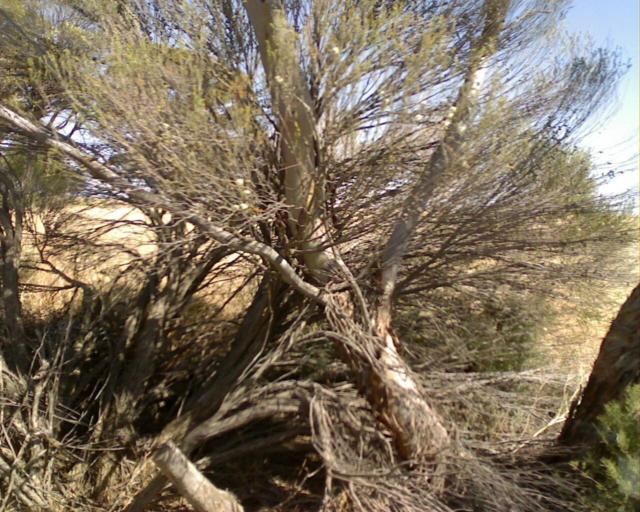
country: AU
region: Western Australia
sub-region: Wongan-Ballidu
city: Wongan Hills
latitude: -30.3843
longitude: 116.7848
